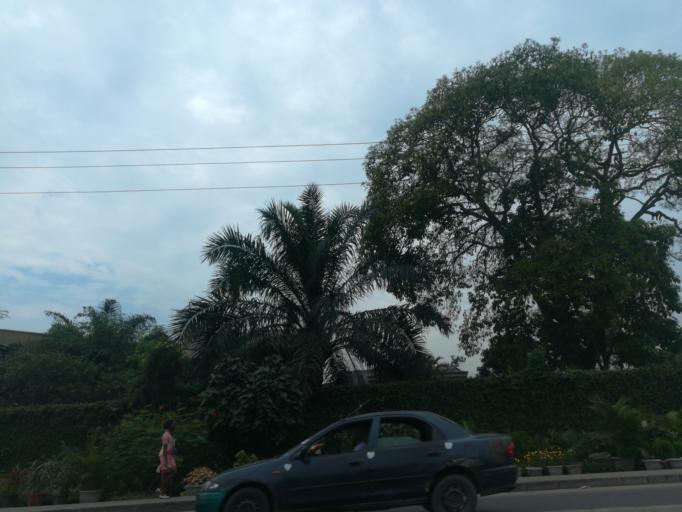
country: NG
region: Rivers
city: Port Harcourt
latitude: 4.8437
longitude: 6.9829
